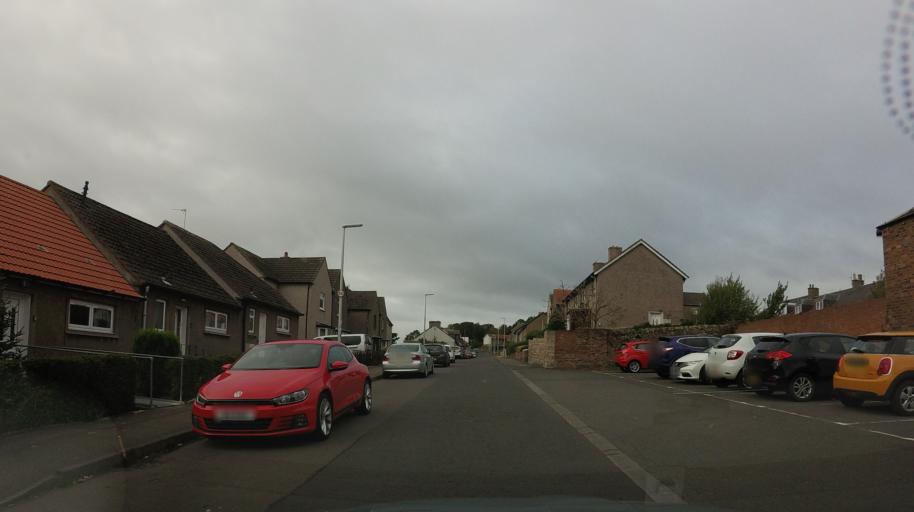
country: GB
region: Scotland
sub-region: Fife
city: Cowdenbeath
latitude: 56.1133
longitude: -3.3457
